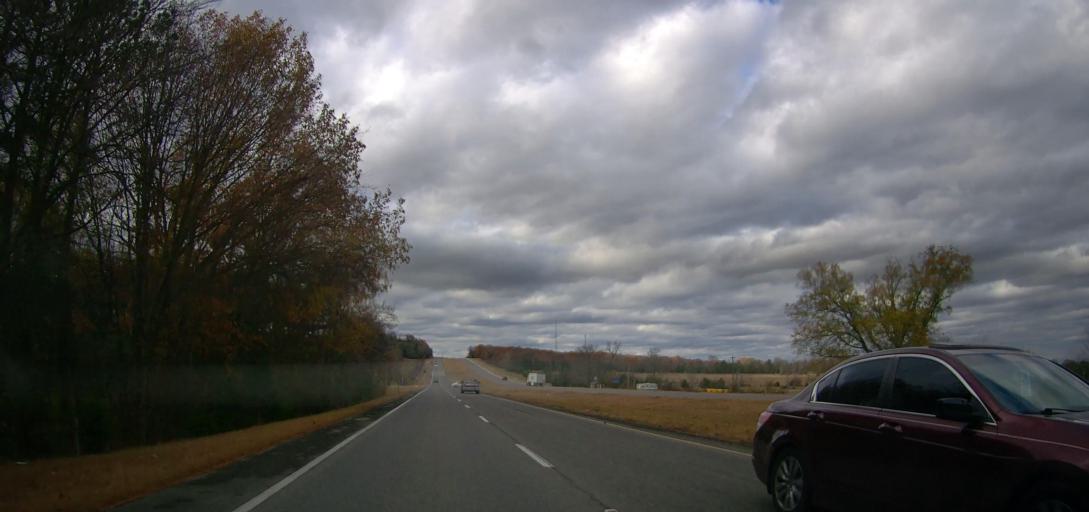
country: US
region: Alabama
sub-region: Morgan County
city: Danville
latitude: 34.3925
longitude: -87.1172
